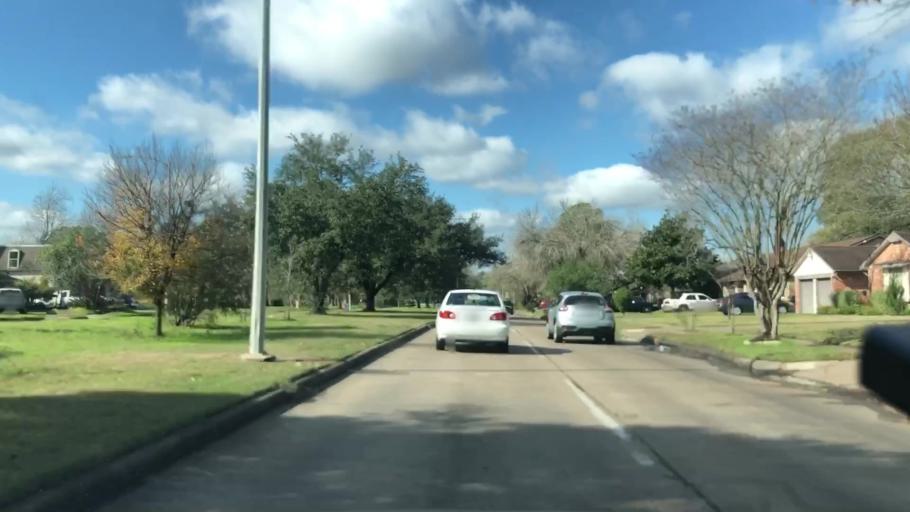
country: US
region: Texas
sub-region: Fort Bend County
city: Missouri City
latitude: 29.6573
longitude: -95.4955
